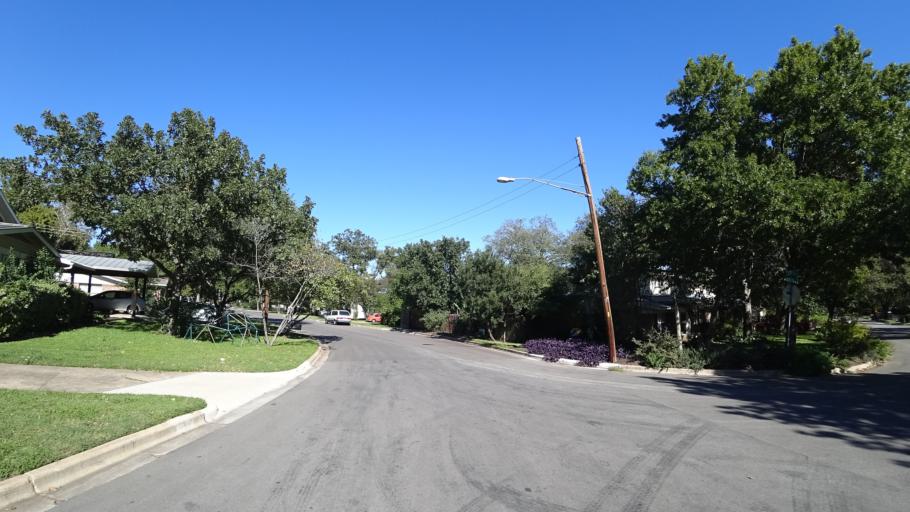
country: US
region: Texas
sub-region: Travis County
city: Austin
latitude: 30.3234
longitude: -97.7502
